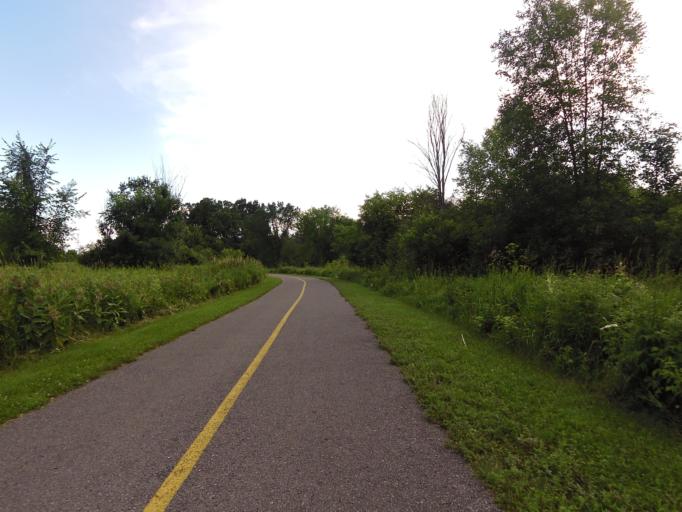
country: CA
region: Ontario
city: Bells Corners
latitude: 45.3355
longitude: -75.8866
